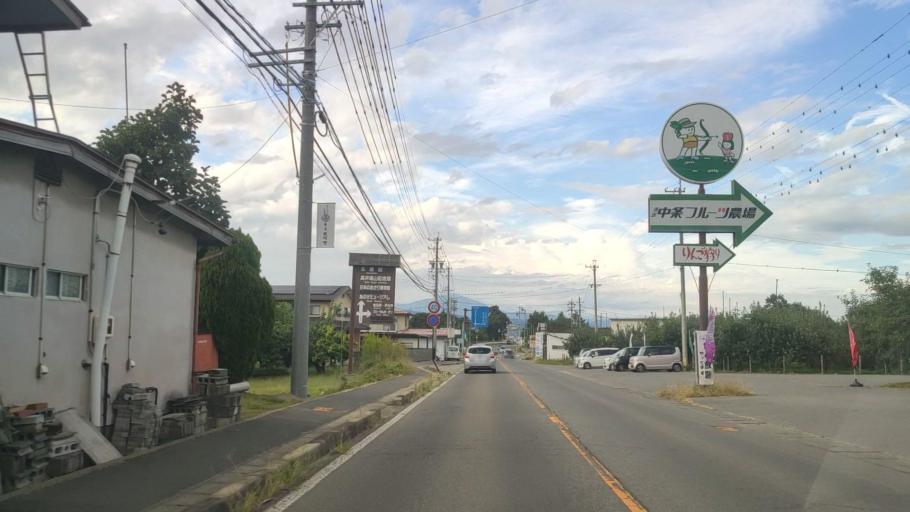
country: JP
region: Nagano
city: Suzaka
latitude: 36.6853
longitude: 138.3158
